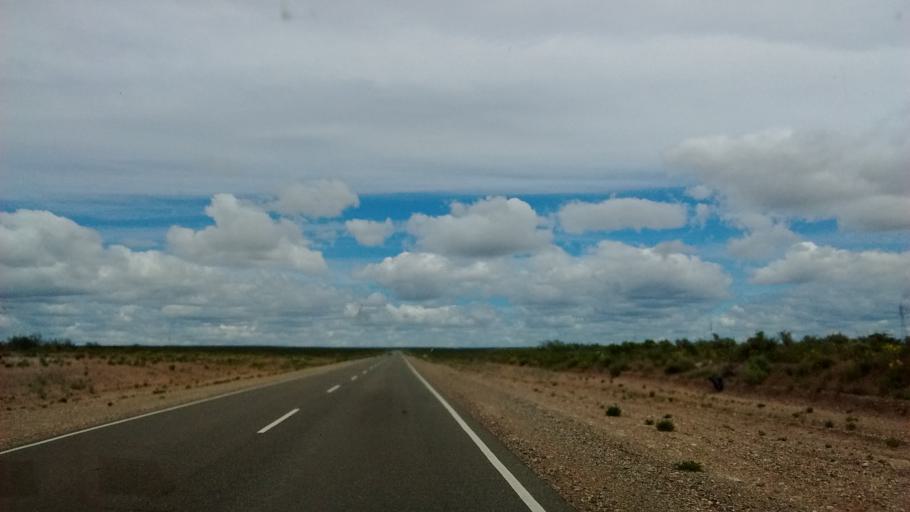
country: AR
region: Neuquen
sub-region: Departamento de Picun Leufu
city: Picun Leufu
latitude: -39.7419
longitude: -69.6041
